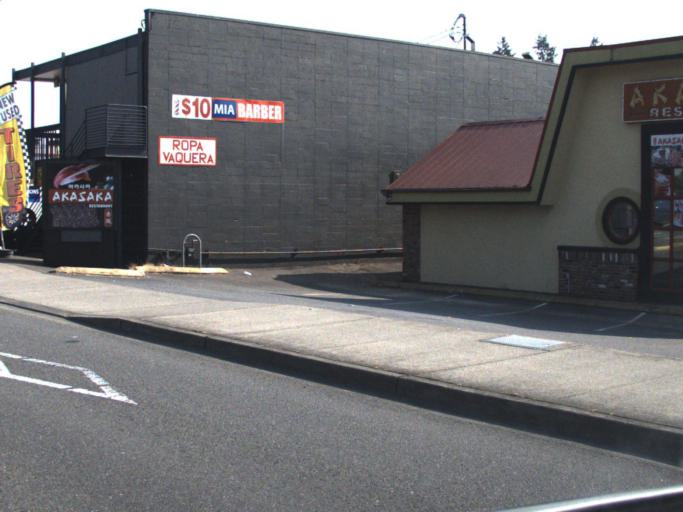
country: US
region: Washington
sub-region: King County
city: Federal Way
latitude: 47.3213
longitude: -122.3133
